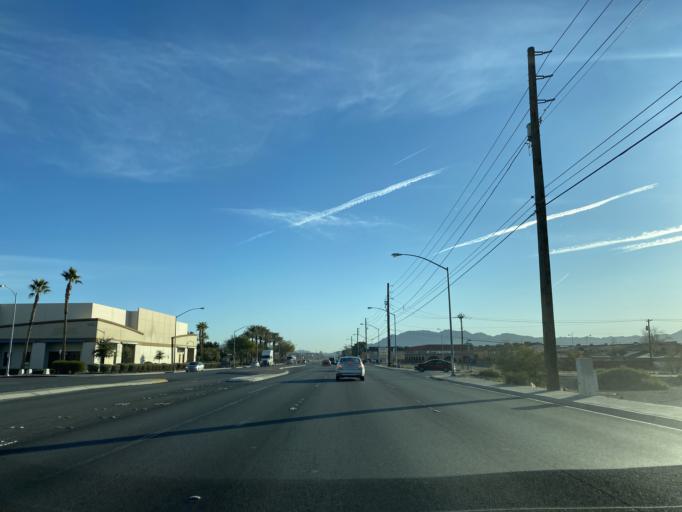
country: US
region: Nevada
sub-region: Clark County
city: Nellis Air Force Base
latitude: 36.2403
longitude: -115.0728
